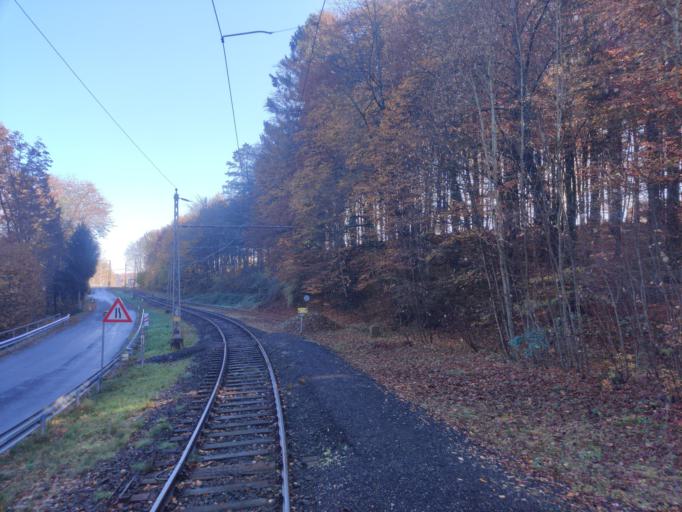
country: AT
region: Styria
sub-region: Politischer Bezirk Suedoststeiermark
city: Maierdorf
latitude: 46.9204
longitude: 15.8478
